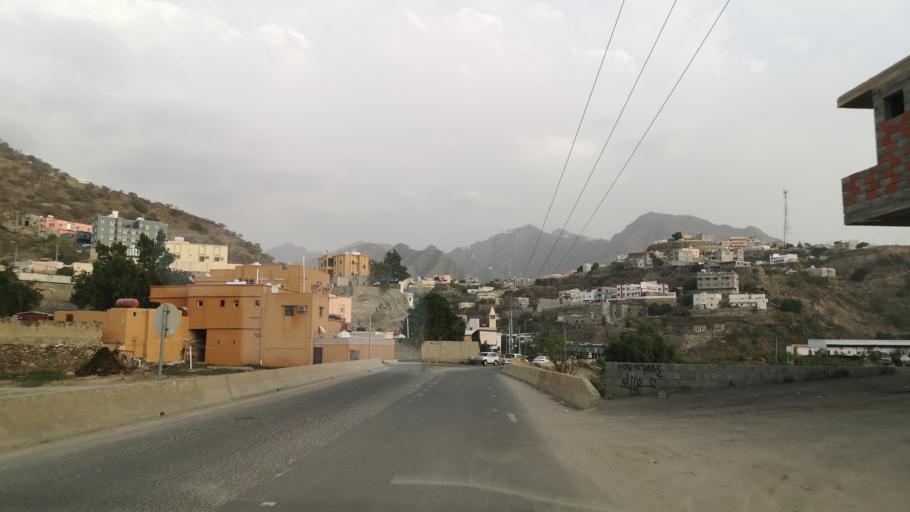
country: YE
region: Sa'dah
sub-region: Monabbih
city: Suq al Khamis
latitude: 17.3511
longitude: 43.1350
